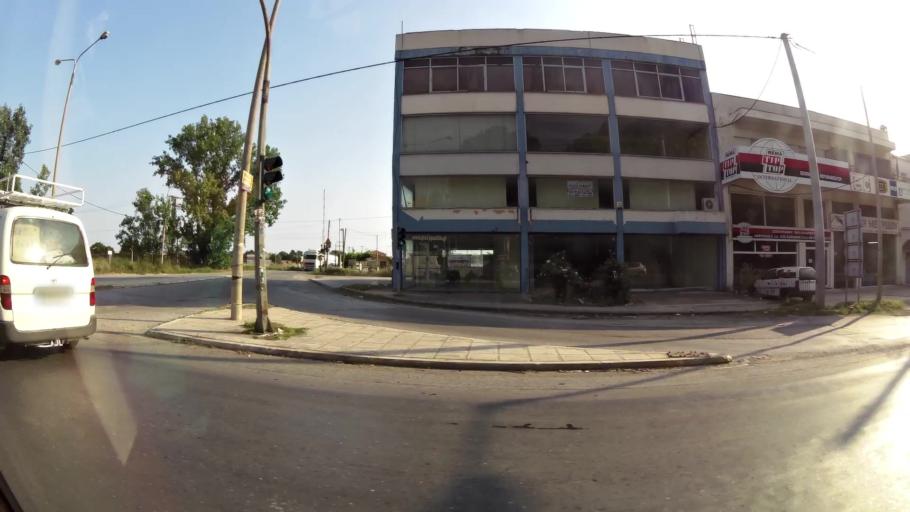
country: GR
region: Central Macedonia
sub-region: Nomos Thessalonikis
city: Diavata
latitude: 40.6799
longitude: 22.8670
